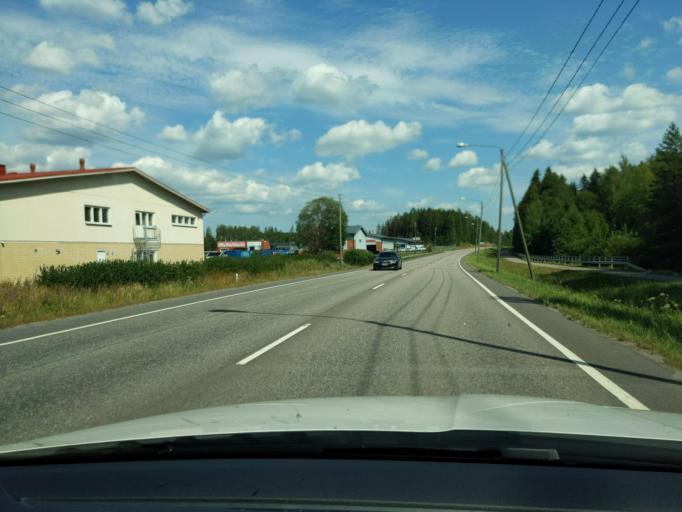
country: FI
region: Uusimaa
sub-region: Helsinki
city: Maentsaelae
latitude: 60.6152
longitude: 25.2740
